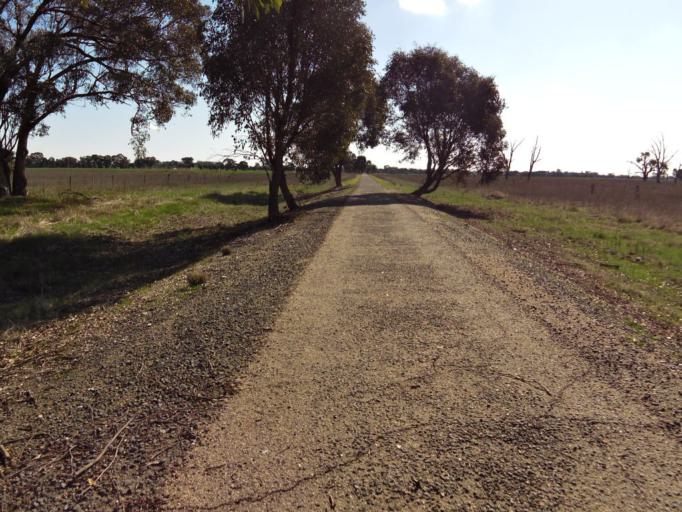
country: AU
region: New South Wales
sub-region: Corowa Shire
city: Corowa
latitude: -36.0204
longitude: 146.4220
